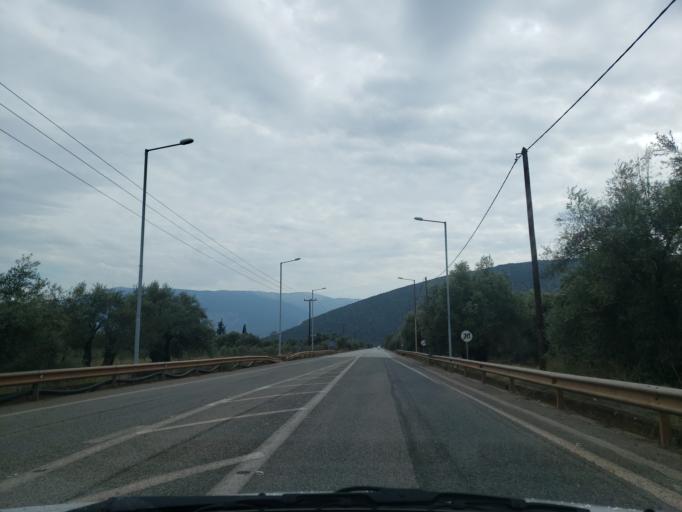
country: GR
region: Central Greece
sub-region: Nomos Fokidos
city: Amfissa
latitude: 38.4917
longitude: 22.4154
